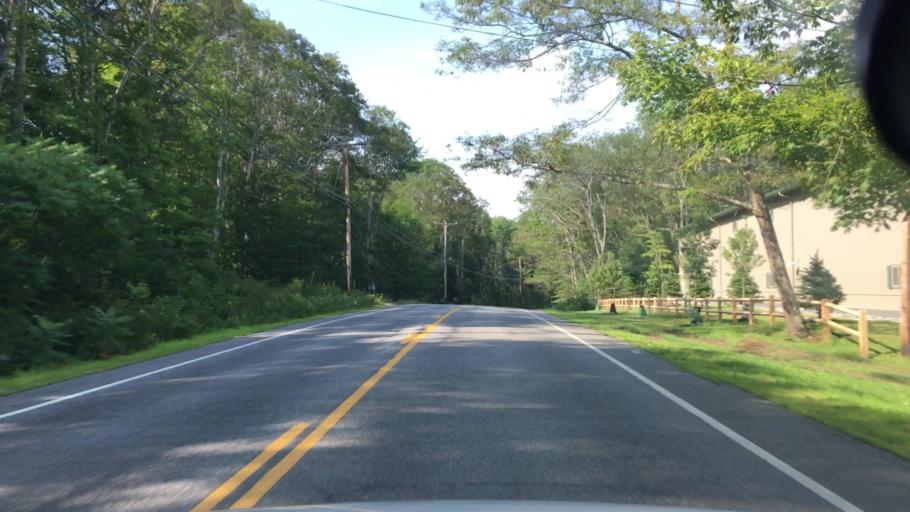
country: US
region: Maine
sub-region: Cumberland County
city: Harpswell Center
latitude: 43.8312
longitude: -69.9174
